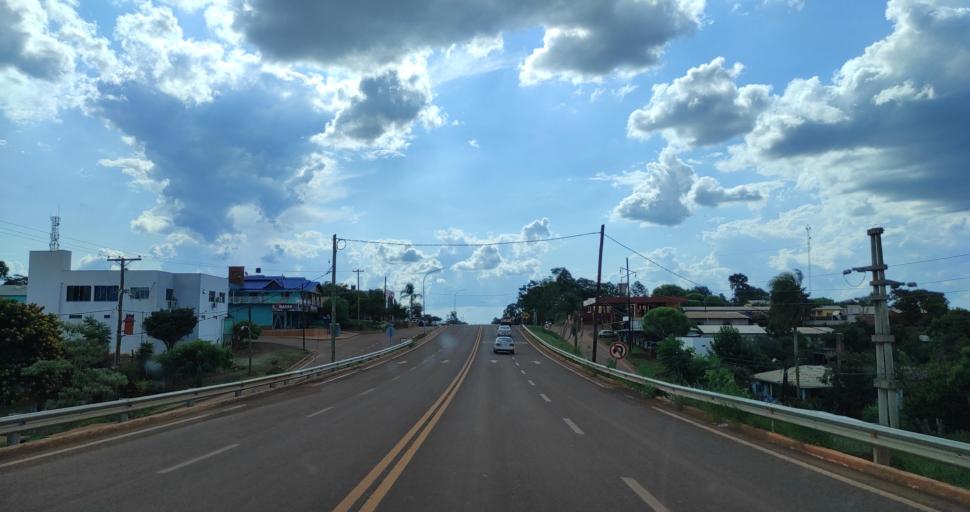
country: AR
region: Misiones
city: Bernardo de Irigoyen
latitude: -26.2950
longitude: -53.7539
